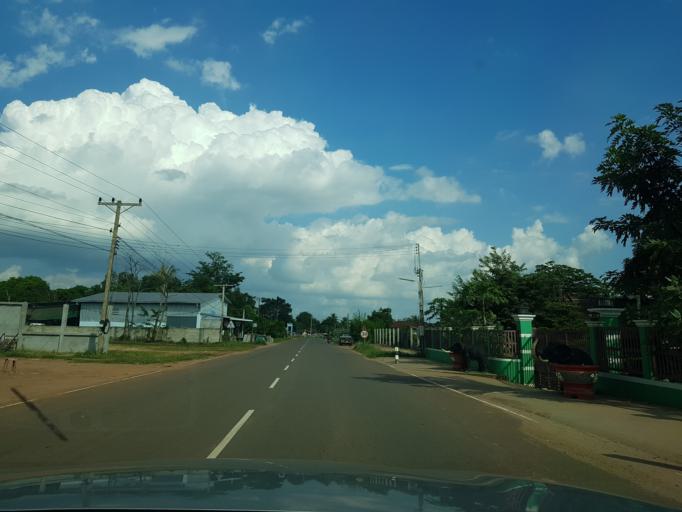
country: TH
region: Nong Khai
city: Pho Tak
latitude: 17.9833
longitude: 102.4443
